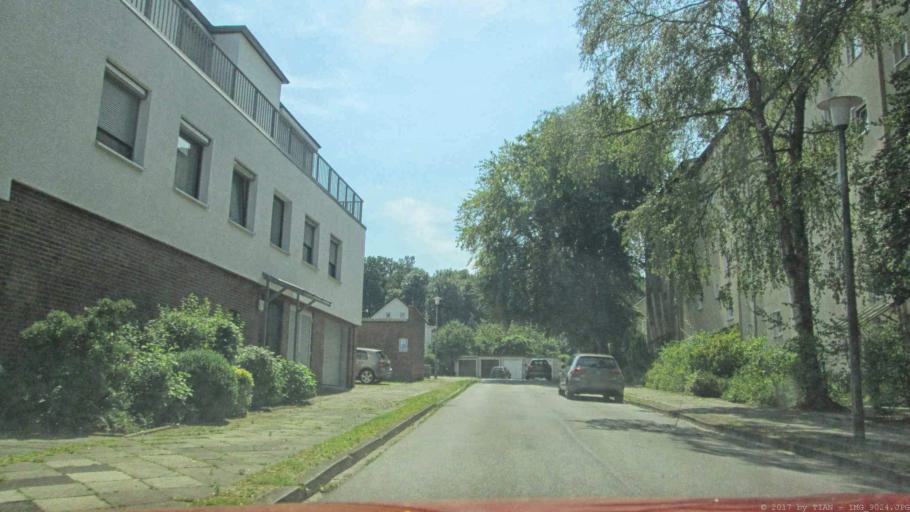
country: DE
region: Lower Saxony
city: Wolfsburg
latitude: 52.4195
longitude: 10.8103
